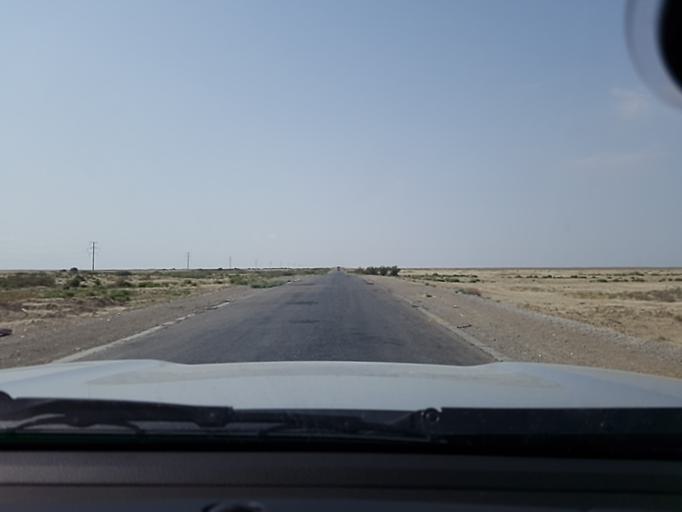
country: TM
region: Balkan
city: Gumdag
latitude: 38.9723
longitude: 54.5879
